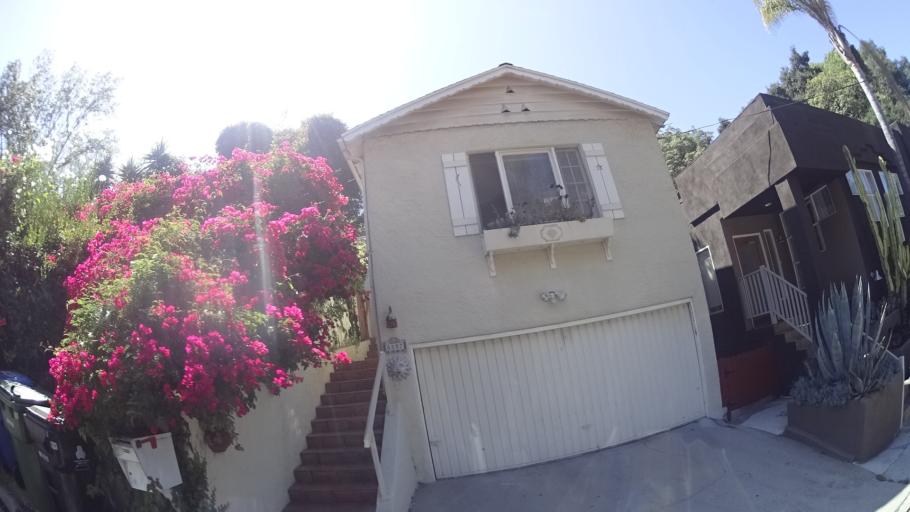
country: US
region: California
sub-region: Los Angeles County
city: West Hollywood
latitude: 34.1096
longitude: -118.3875
